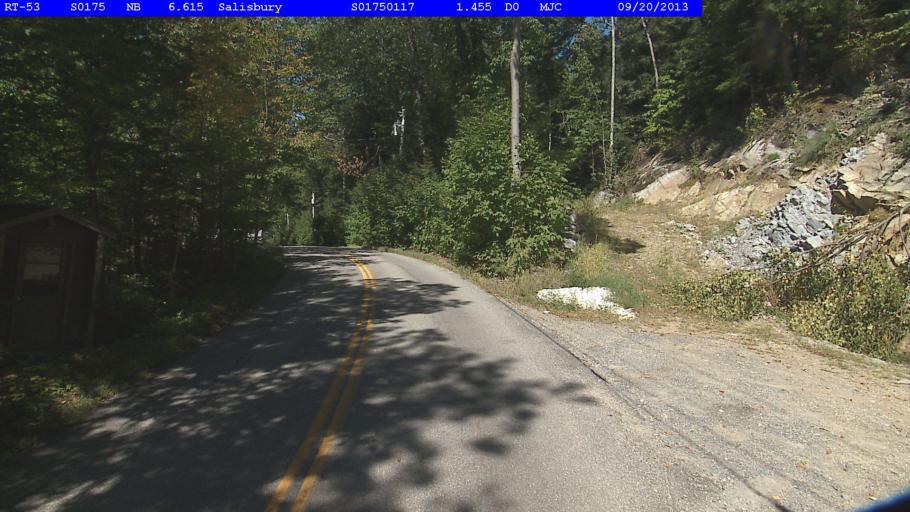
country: US
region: Vermont
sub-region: Rutland County
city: Brandon
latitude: 43.9180
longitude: -73.0694
